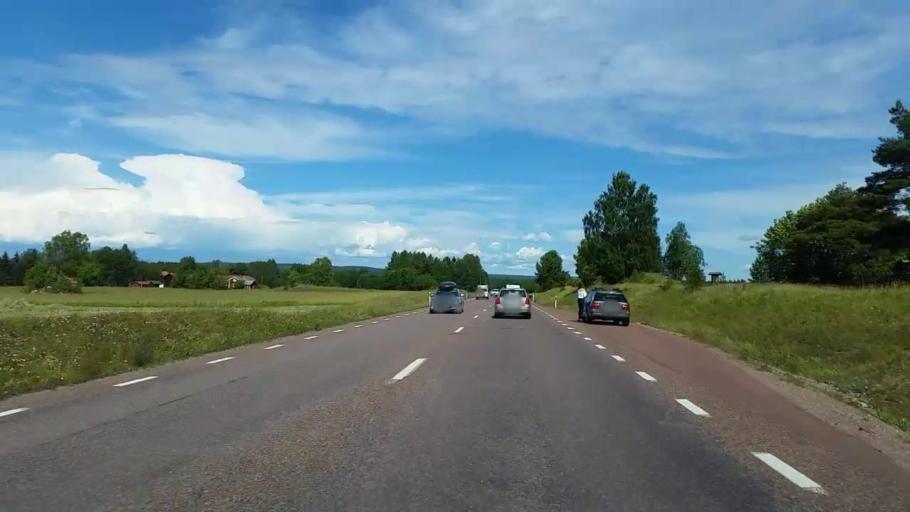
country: SE
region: Dalarna
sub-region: Rattviks Kommun
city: Raettvik
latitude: 60.9347
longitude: 15.2301
